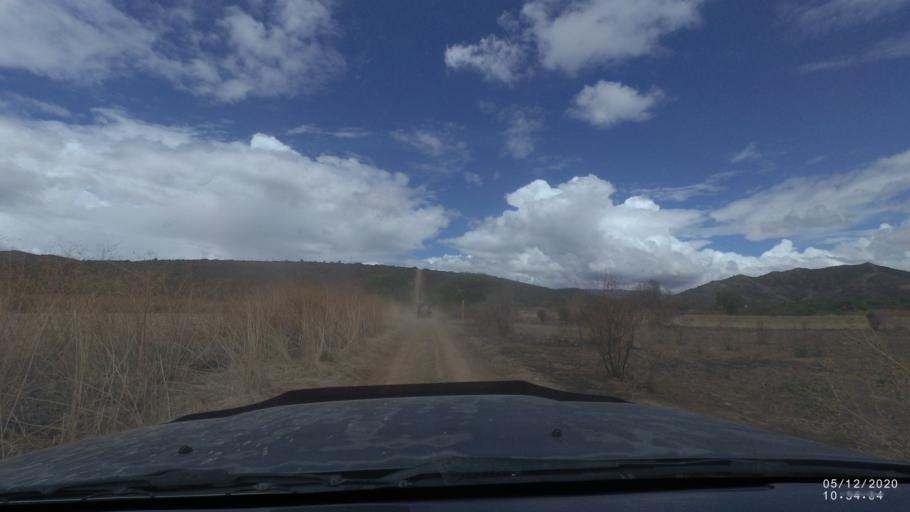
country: BO
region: Cochabamba
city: Sipe Sipe
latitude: -17.5457
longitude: -66.2766
